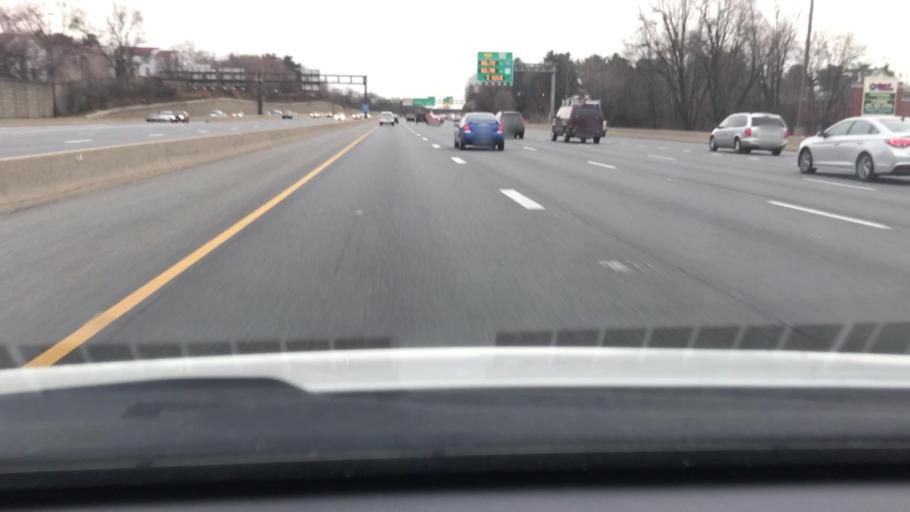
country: US
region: Maryland
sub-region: Montgomery County
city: Gaithersburg
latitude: 39.1302
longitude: -77.2055
